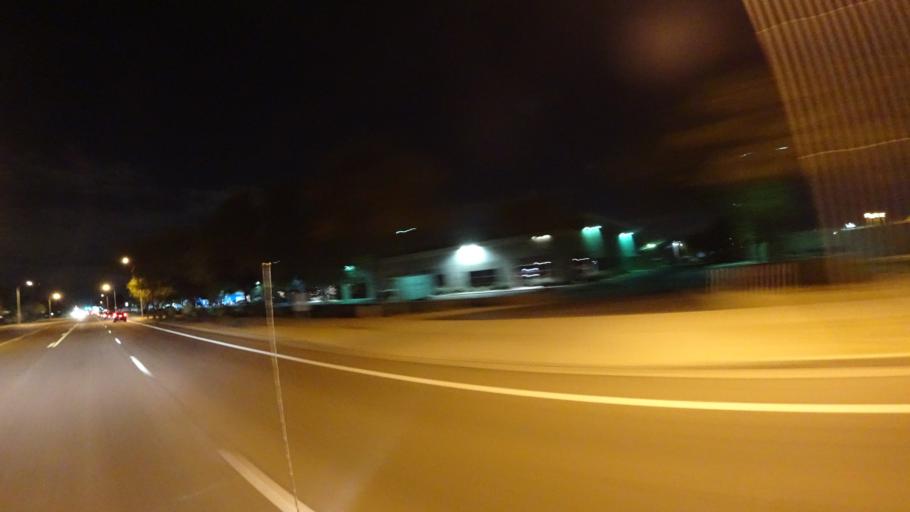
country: US
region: Arizona
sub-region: Maricopa County
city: Guadalupe
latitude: 33.3734
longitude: -111.9459
